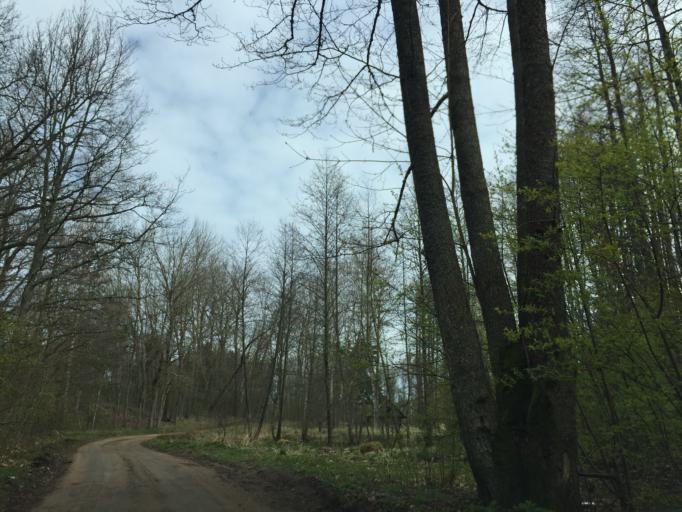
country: LV
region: Salacgrivas
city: Salacgriva
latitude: 57.5218
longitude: 24.3794
